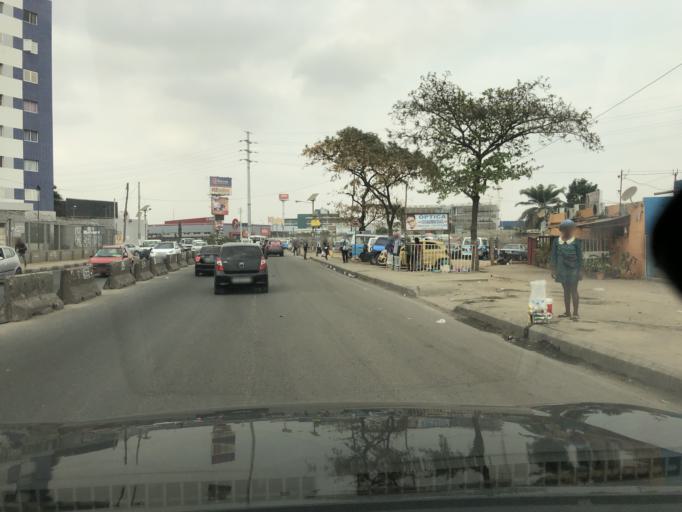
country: AO
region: Luanda
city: Luanda
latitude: -8.8476
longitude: 13.2847
